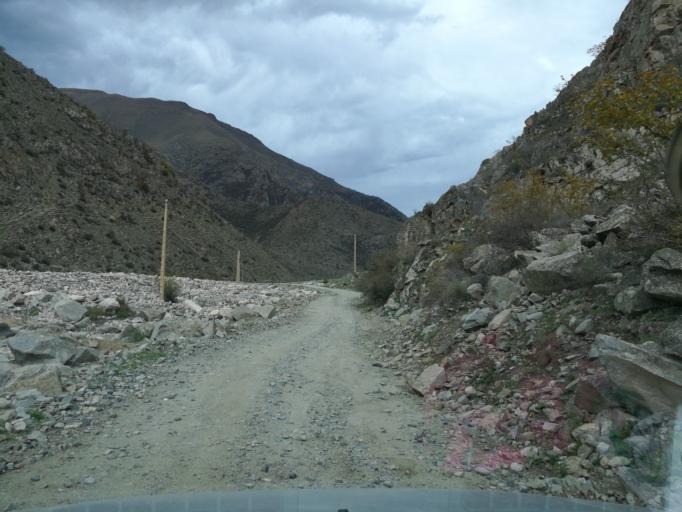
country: IR
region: Mazandaran
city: `Abbasabad
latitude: 36.4299
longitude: 51.0413
